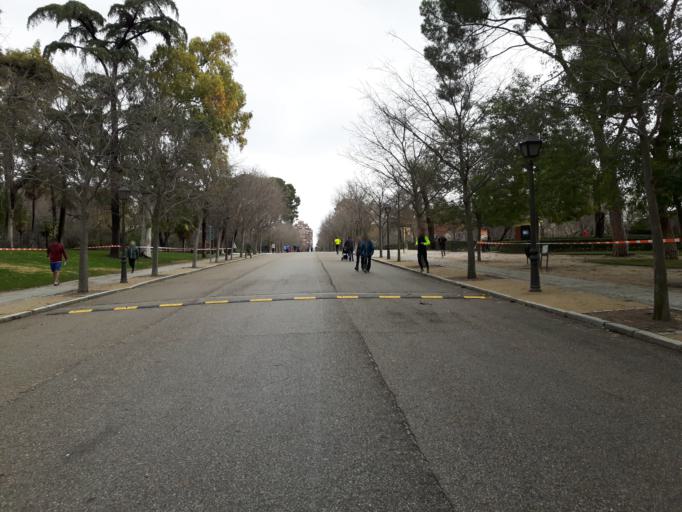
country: ES
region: Madrid
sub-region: Provincia de Madrid
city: Retiro
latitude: 40.4102
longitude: -3.6861
